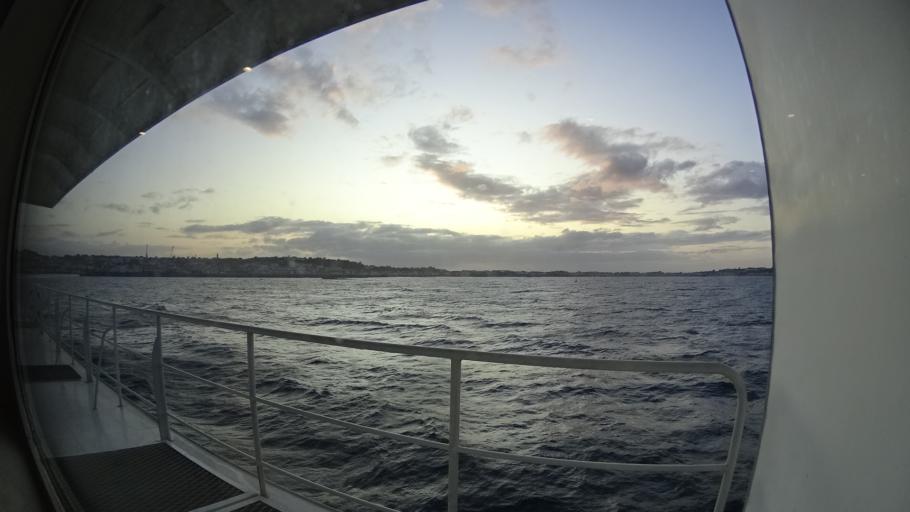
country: GG
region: St Peter Port
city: Saint Peter Port
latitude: 49.4587
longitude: -2.5162
